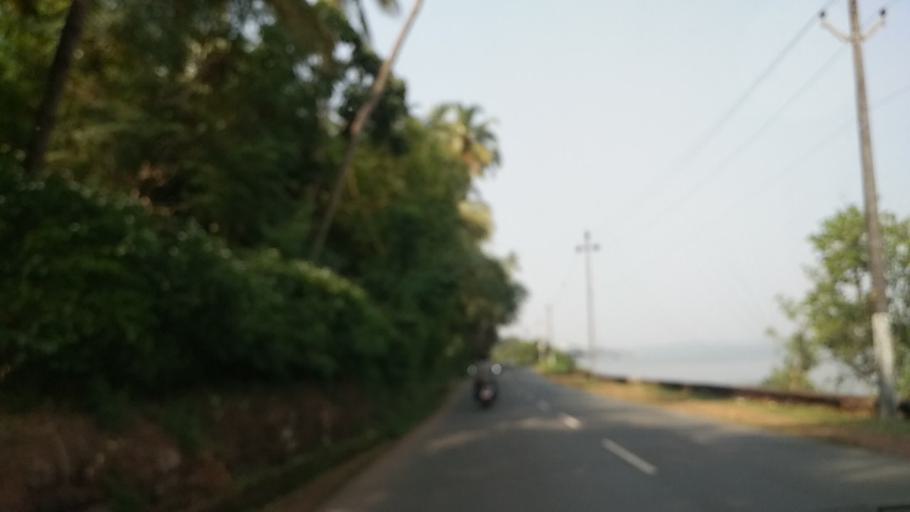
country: IN
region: Goa
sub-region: North Goa
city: Bambolim
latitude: 15.4998
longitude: 73.8888
